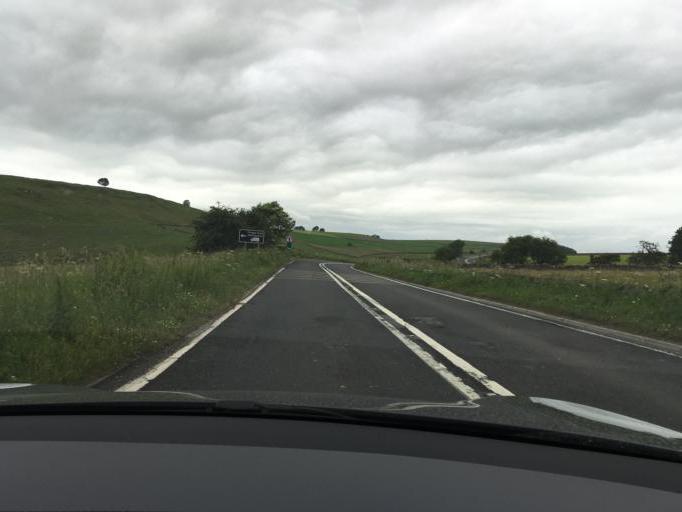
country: GB
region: England
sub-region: Derbyshire
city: Tideswell
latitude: 53.2940
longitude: -1.7842
